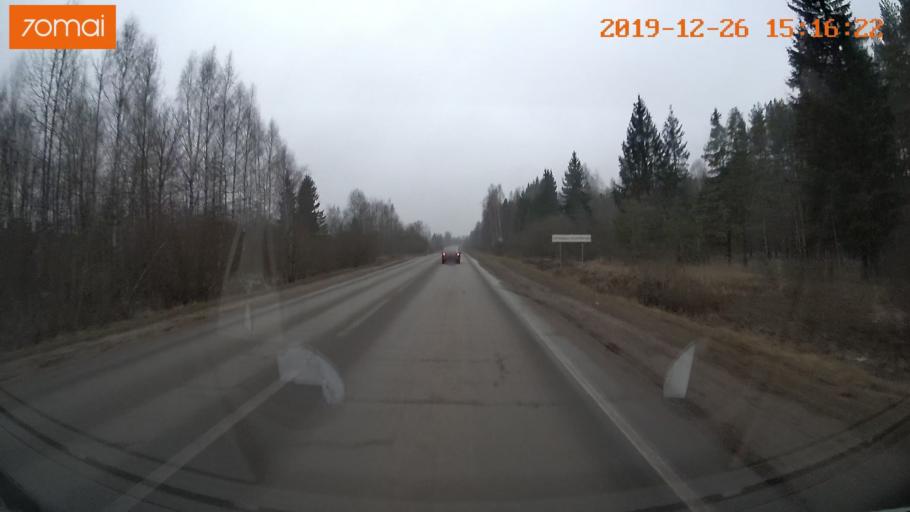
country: RU
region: Jaroslavl
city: Rybinsk
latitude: 58.0872
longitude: 38.8667
